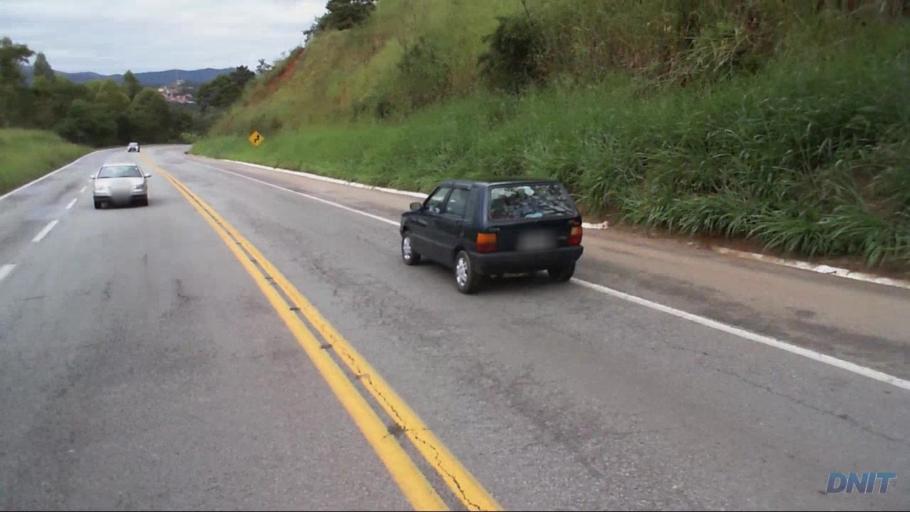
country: BR
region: Minas Gerais
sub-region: Barao De Cocais
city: Barao de Cocais
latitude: -19.8354
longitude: -43.3698
